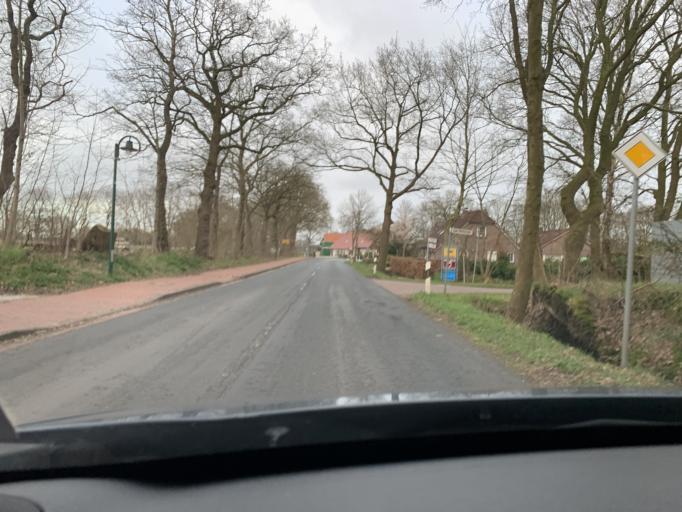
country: DE
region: Lower Saxony
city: Detern
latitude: 53.2549
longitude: 7.7139
